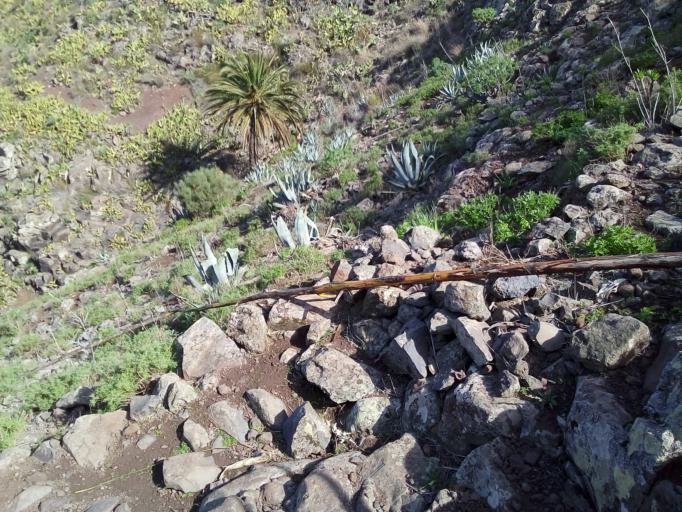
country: ES
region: Canary Islands
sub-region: Provincia de Santa Cruz de Tenerife
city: Vallehermosa
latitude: 28.1169
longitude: -17.2960
